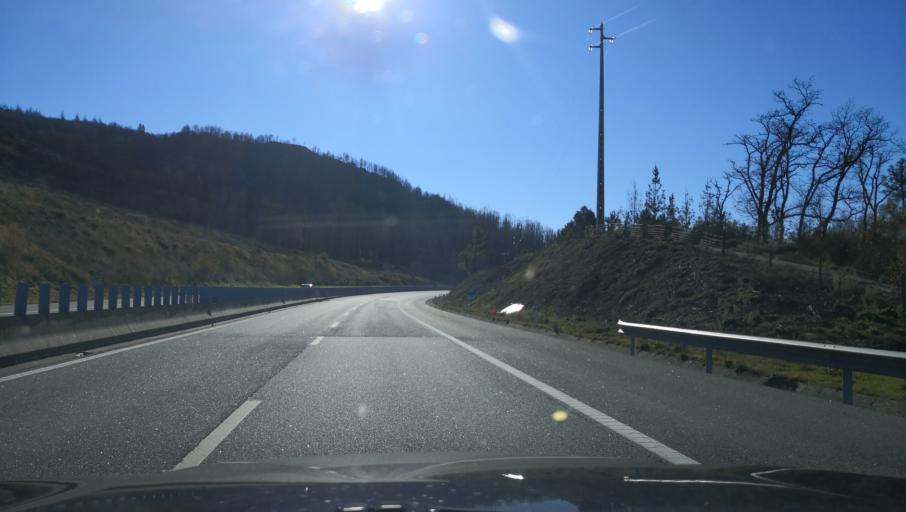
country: PT
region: Viseu
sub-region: Vouzela
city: Vouzela
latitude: 40.7034
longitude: -8.1235
